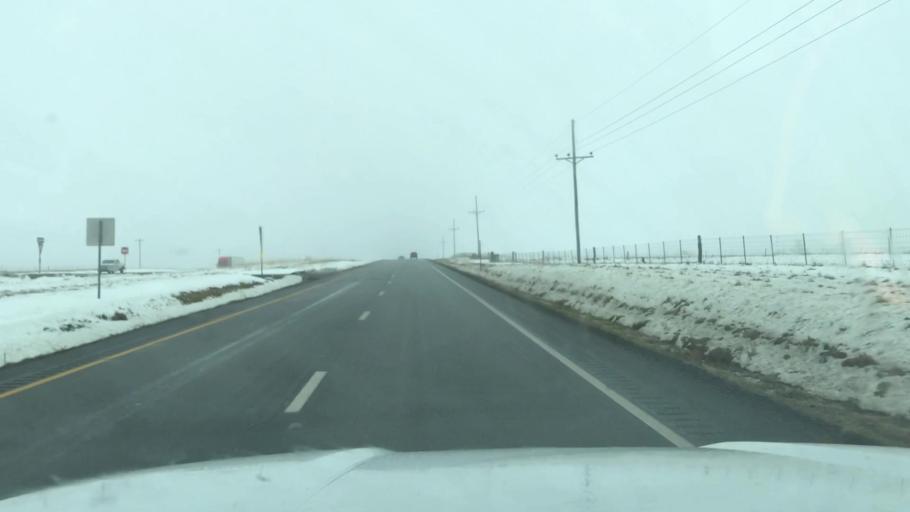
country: US
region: Missouri
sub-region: Clinton County
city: Cameron
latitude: 39.7538
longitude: -94.2774
